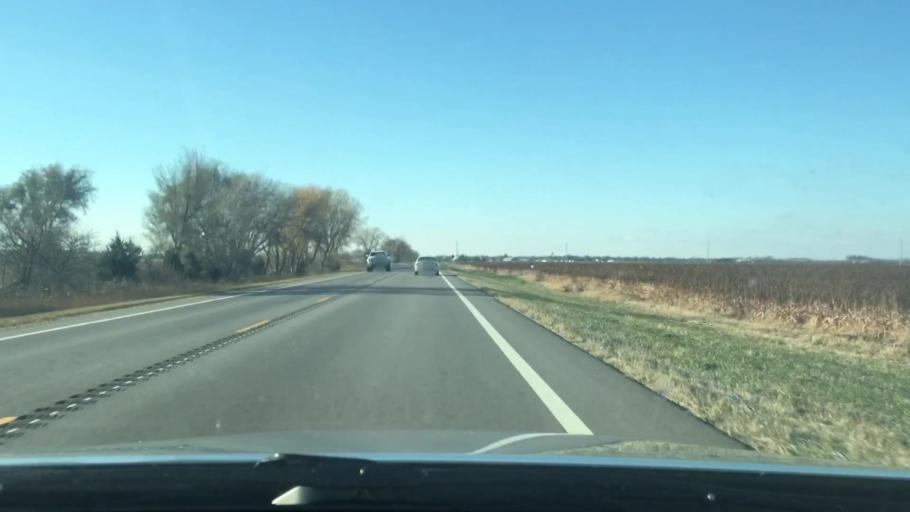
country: US
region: Kansas
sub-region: Reno County
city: Nickerson
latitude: 38.1274
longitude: -98.0545
